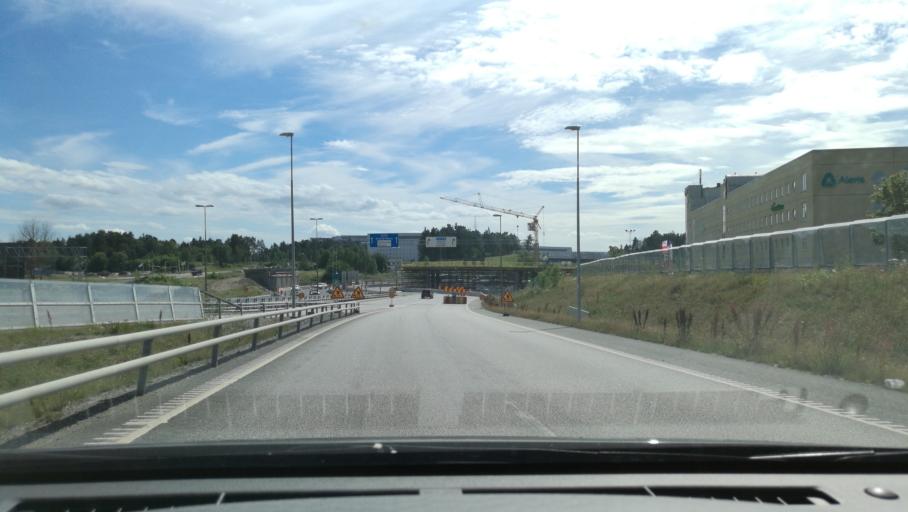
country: SE
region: Stockholm
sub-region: Stockholms Kommun
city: Kista
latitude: 59.3873
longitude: 17.9393
